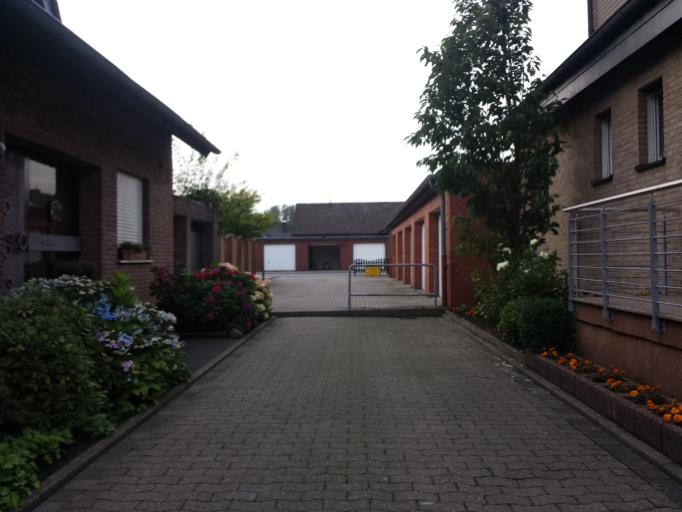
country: DE
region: North Rhine-Westphalia
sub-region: Regierungsbezirk Detmold
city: Harsewinkel
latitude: 51.9703
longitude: 8.2422
